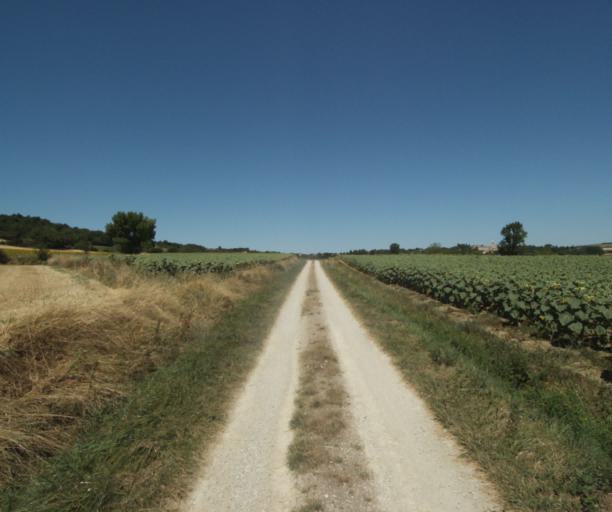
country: FR
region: Midi-Pyrenees
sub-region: Departement de la Haute-Garonne
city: Saint-Felix-Lauragais
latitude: 43.4692
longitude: 1.9238
